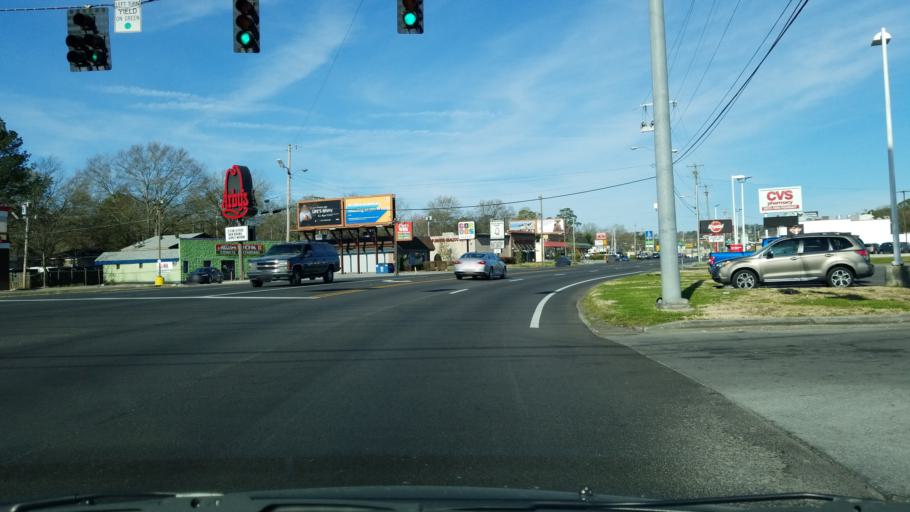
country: US
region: Tennessee
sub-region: Hamilton County
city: East Ridge
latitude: 35.0100
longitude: -85.2201
